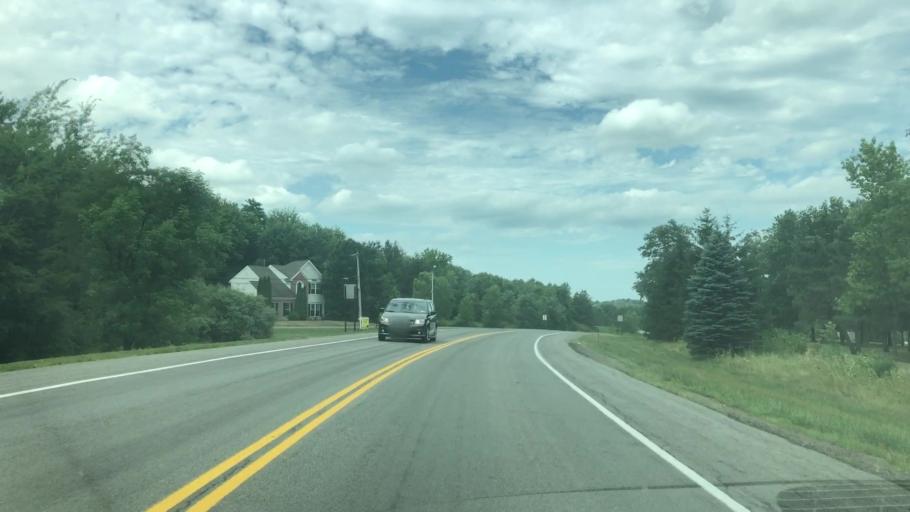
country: US
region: New York
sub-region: Wayne County
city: Macedon
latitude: 43.1239
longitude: -77.3363
